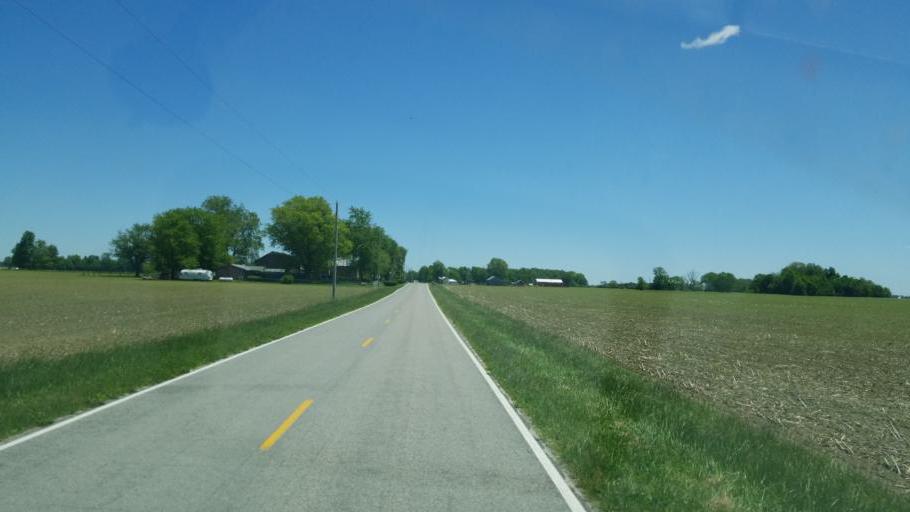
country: US
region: Indiana
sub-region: Randolph County
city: Union City
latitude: 40.2817
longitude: -84.7713
